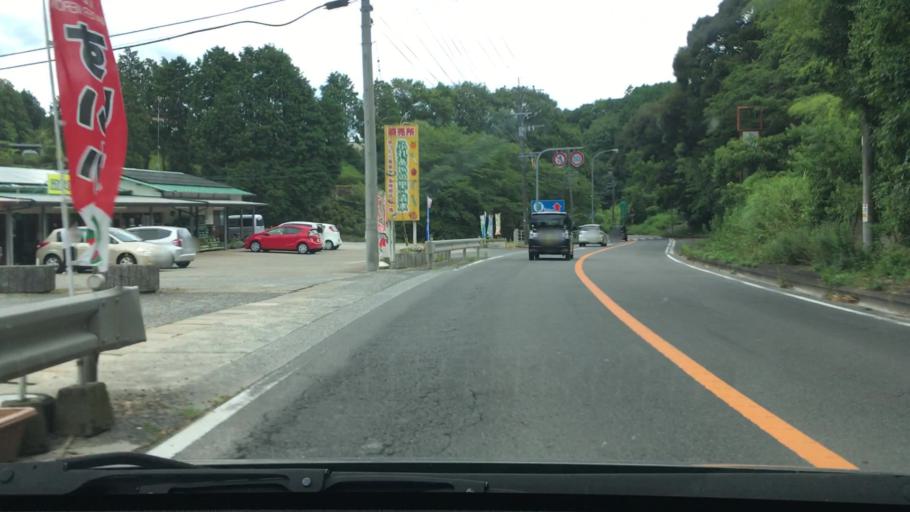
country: JP
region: Nagasaki
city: Togitsu
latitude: 32.9795
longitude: 129.7815
